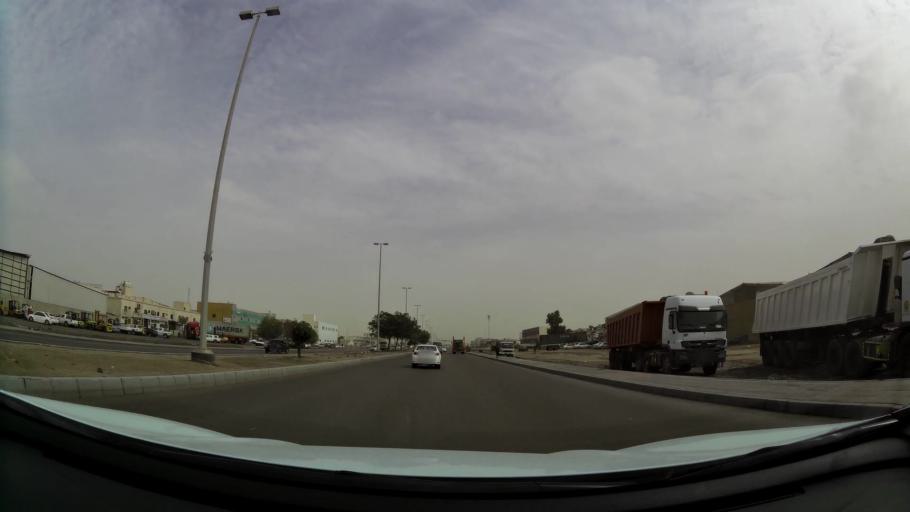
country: AE
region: Abu Dhabi
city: Abu Dhabi
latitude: 24.3595
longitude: 54.5080
